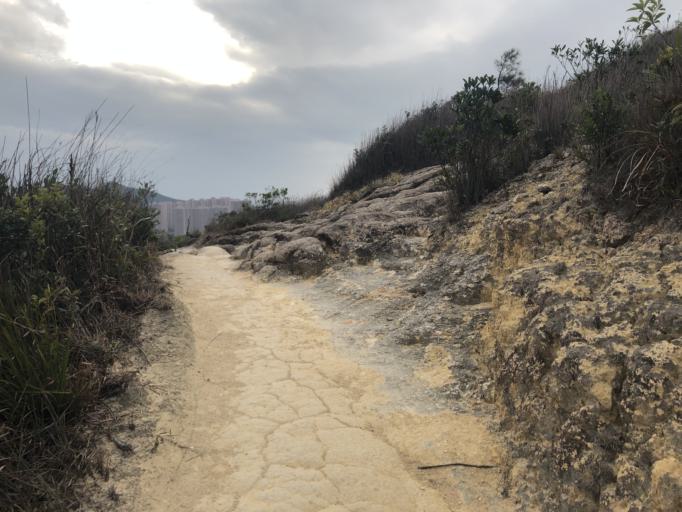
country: HK
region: Wanchai
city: Wan Chai
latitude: 22.2692
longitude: 114.2069
